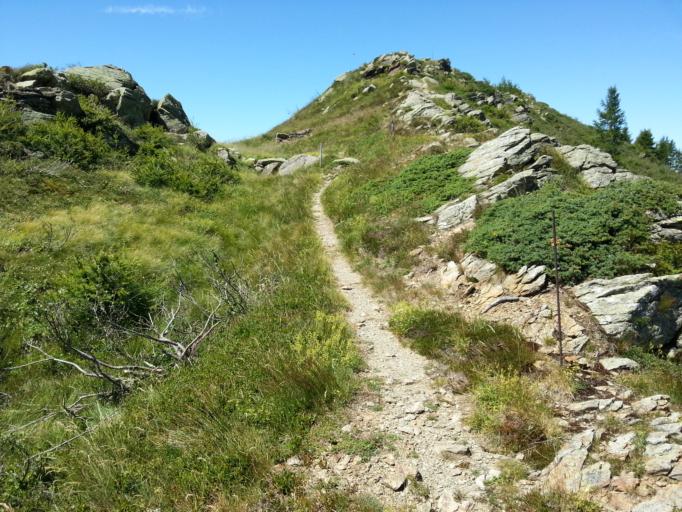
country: CH
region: Ticino
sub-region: Bellinzona District
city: Camorino
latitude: 46.1133
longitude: 9.0449
